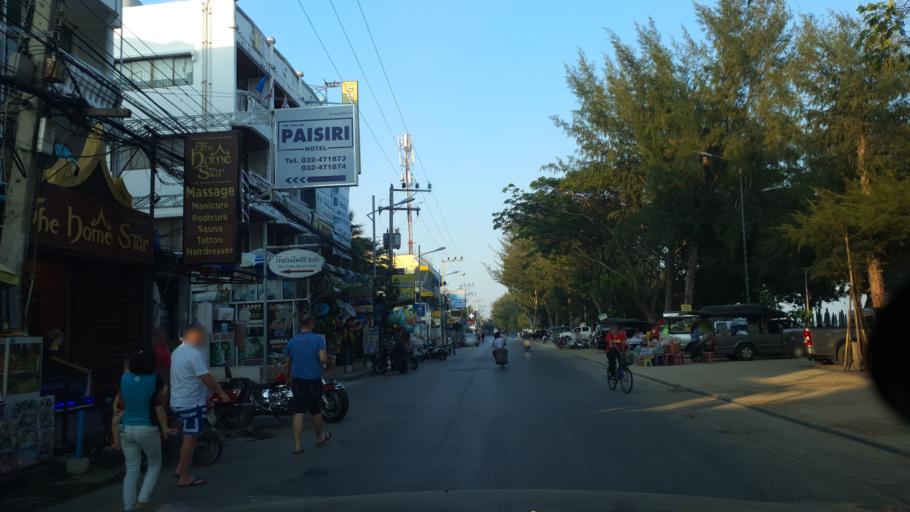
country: TH
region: Phetchaburi
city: Cha-am
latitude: 12.8028
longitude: 99.9869
